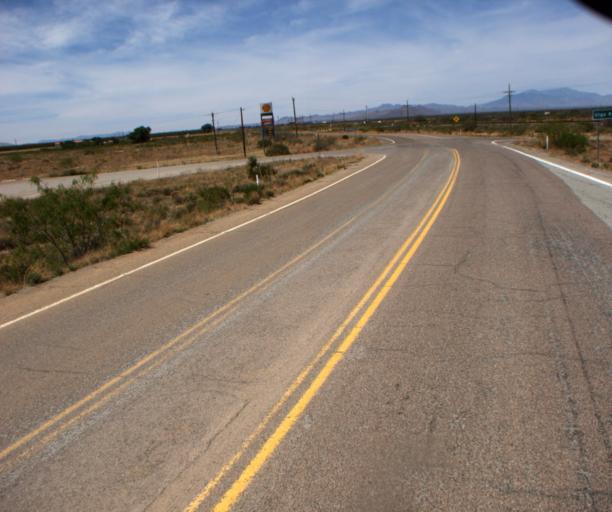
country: US
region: Arizona
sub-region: Cochise County
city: Willcox
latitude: 32.3196
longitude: -109.4515
